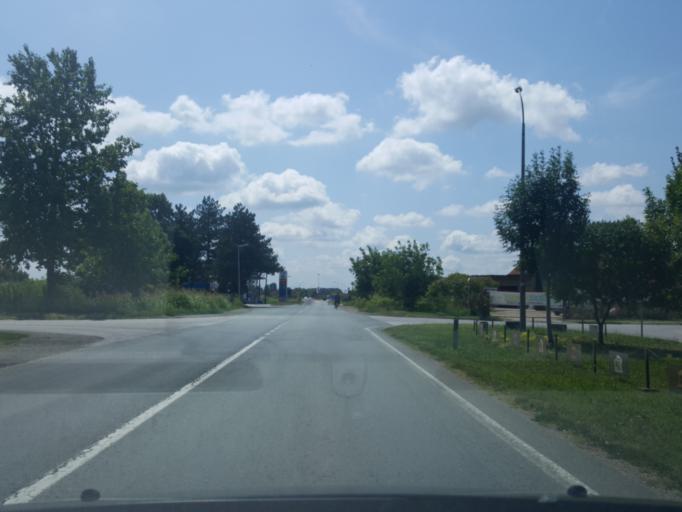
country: RS
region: Autonomna Pokrajina Vojvodina
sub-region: Sremski Okrug
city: Sremska Mitrovica
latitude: 44.9740
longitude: 19.6377
